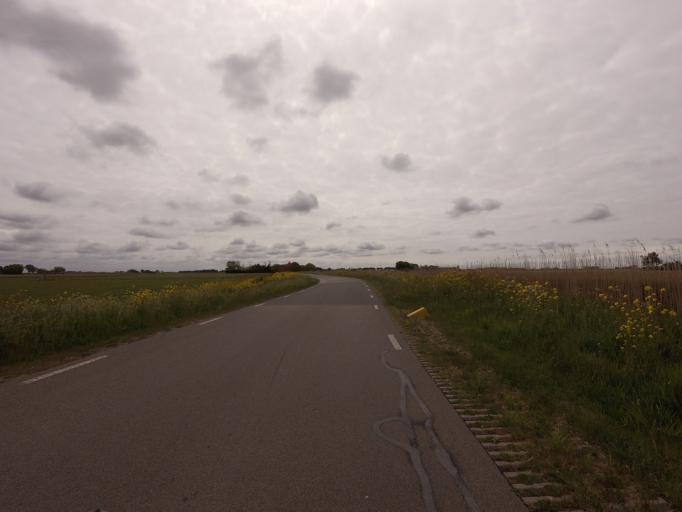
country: NL
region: Friesland
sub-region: Sudwest Fryslan
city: Workum
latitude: 52.9616
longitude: 5.4893
